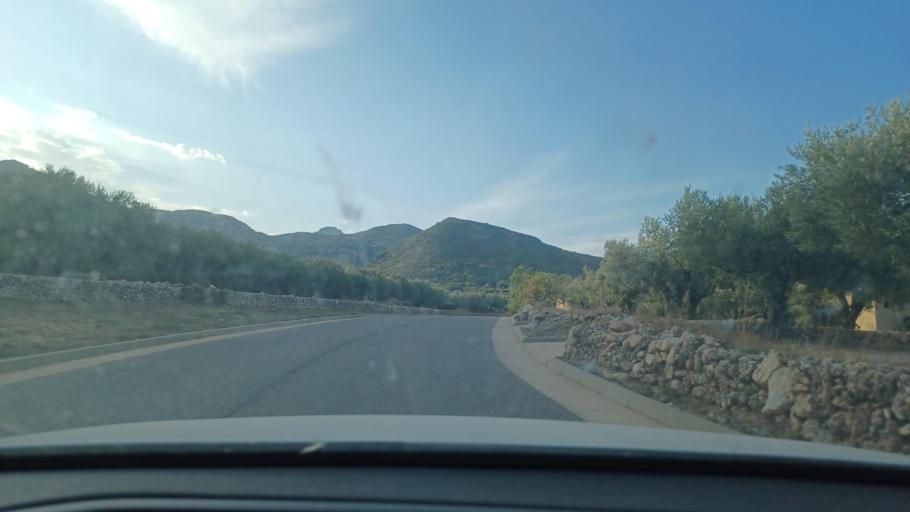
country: ES
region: Catalonia
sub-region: Provincia de Tarragona
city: Mas de Barberans
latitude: 40.7286
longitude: 0.3682
